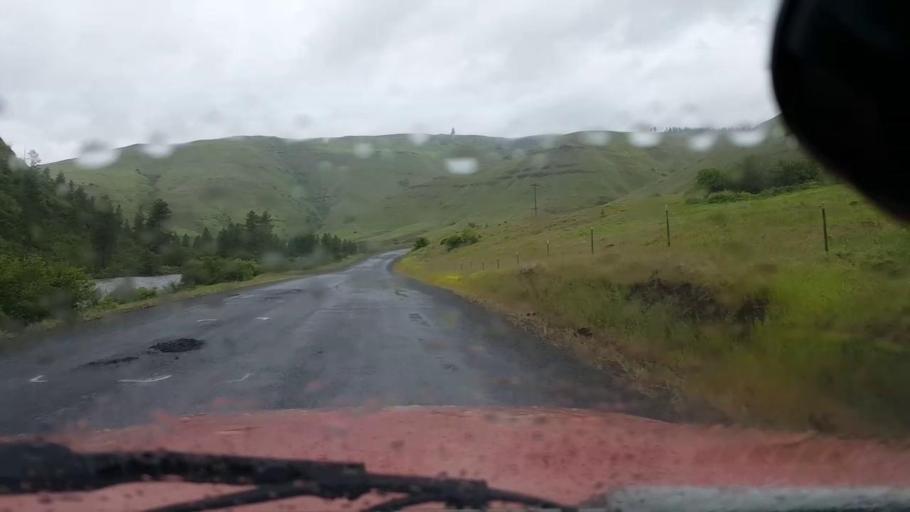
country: US
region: Washington
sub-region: Asotin County
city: Asotin
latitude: 46.0374
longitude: -117.2826
